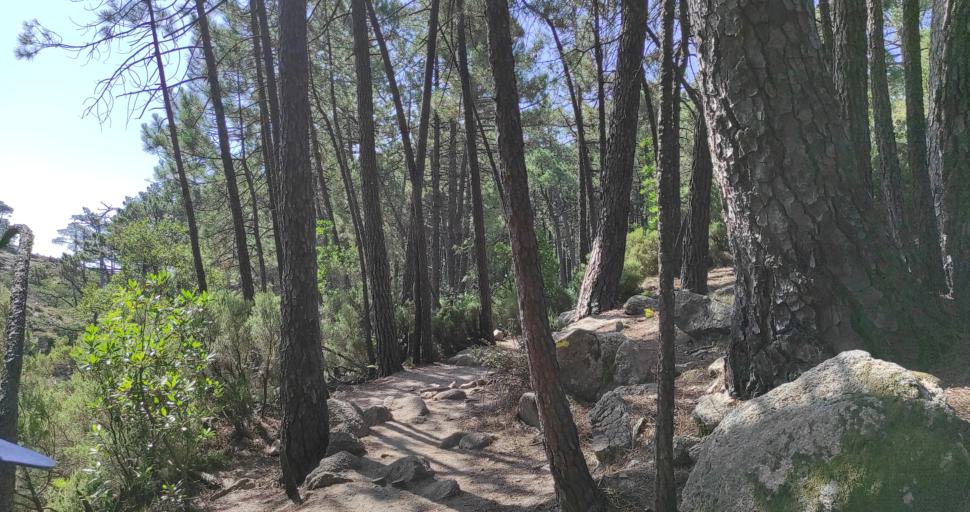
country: FR
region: Corsica
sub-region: Departement de la Corse-du-Sud
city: Zonza
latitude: 41.6857
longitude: 9.2020
